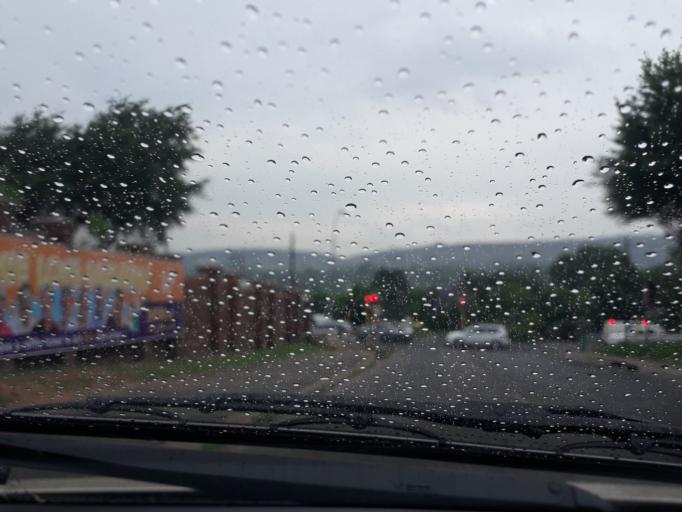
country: ZA
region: Gauteng
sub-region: City of Johannesburg Metropolitan Municipality
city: Modderfontein
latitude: -26.1445
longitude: 28.1073
